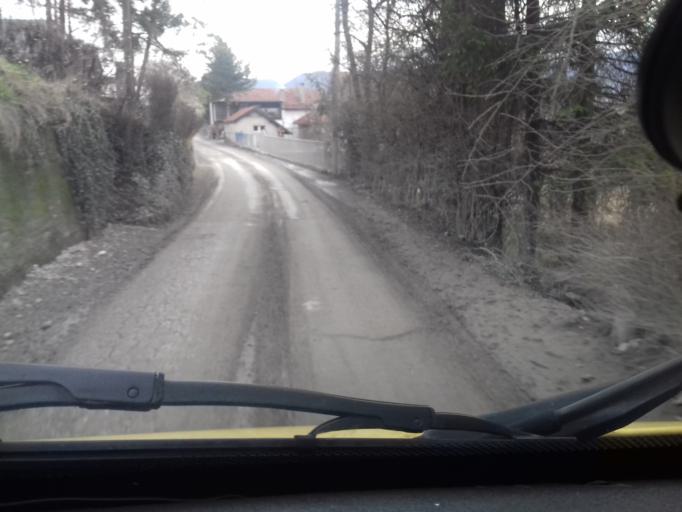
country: BA
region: Federation of Bosnia and Herzegovina
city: Zenica
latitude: 44.2243
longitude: 17.9129
